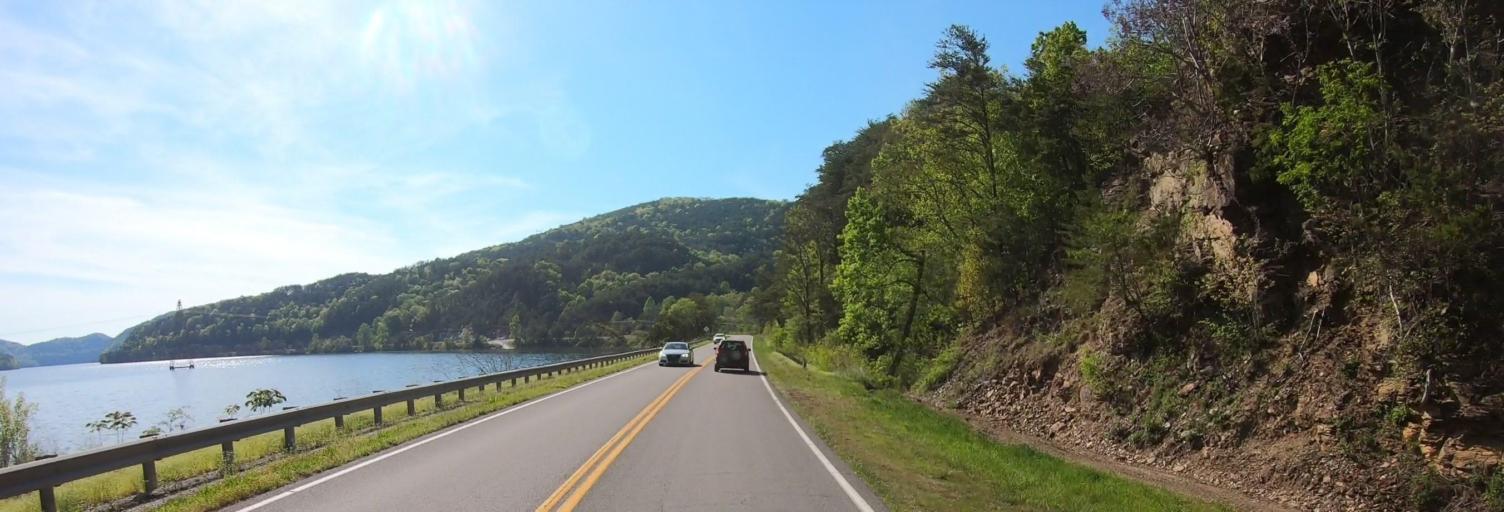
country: US
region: Tennessee
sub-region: Loudon County
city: Greenback
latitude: 35.5563
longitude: -84.0054
